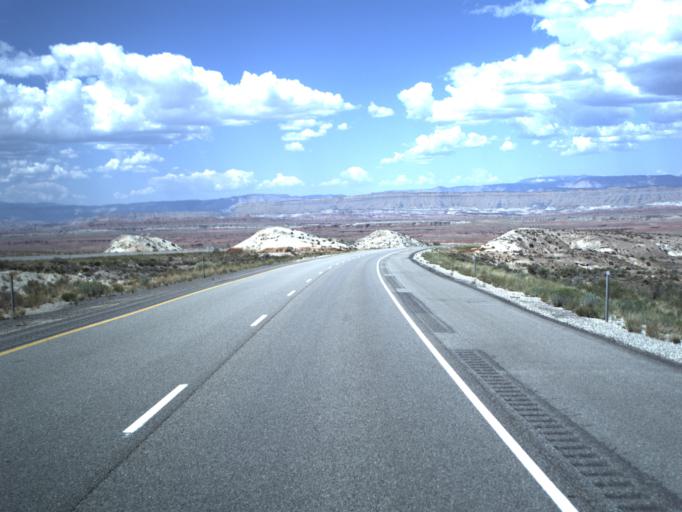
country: US
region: Utah
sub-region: Emery County
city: Ferron
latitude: 38.8444
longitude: -110.9829
